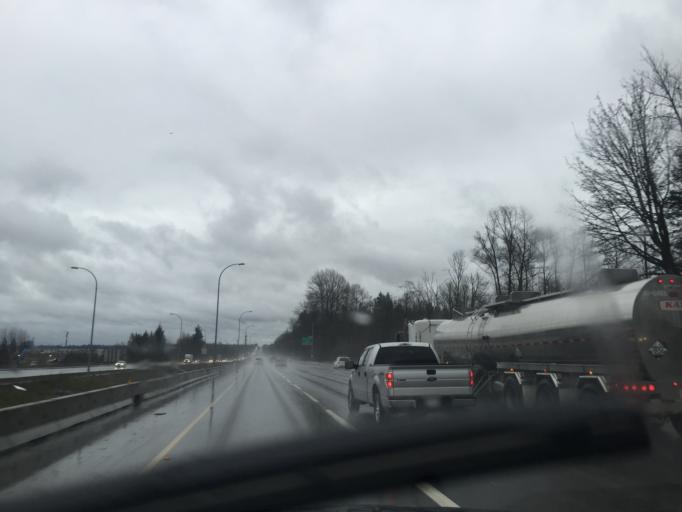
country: CA
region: British Columbia
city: Pitt Meadows
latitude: 49.1769
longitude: -122.7177
